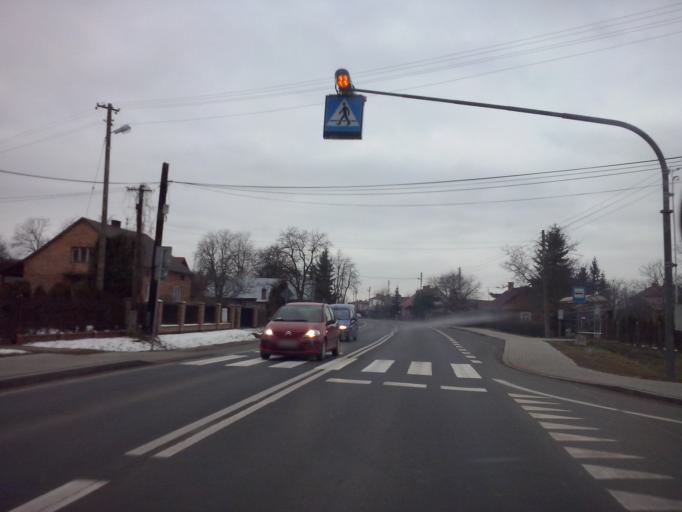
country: PL
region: Subcarpathian Voivodeship
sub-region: Powiat nizanski
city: Raclawice
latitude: 50.5132
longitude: 22.1658
